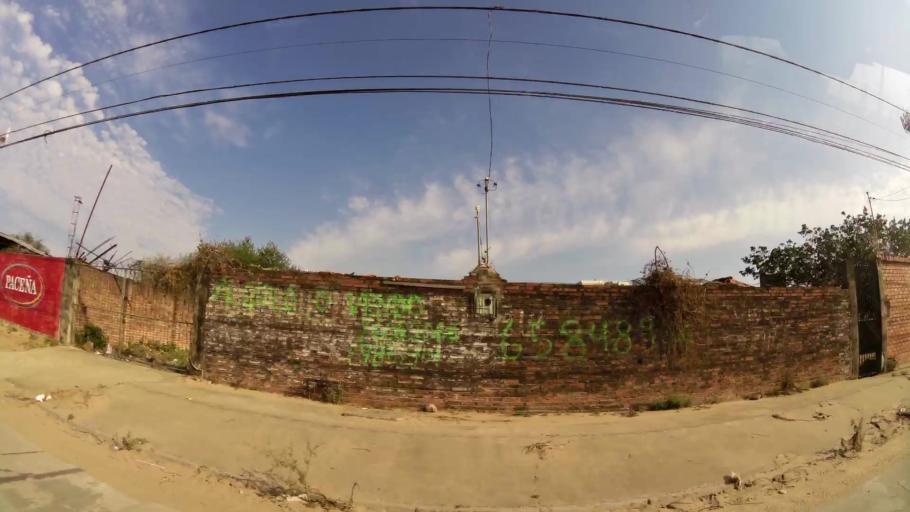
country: BO
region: Santa Cruz
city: Santa Cruz de la Sierra
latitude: -17.7411
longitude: -63.1457
